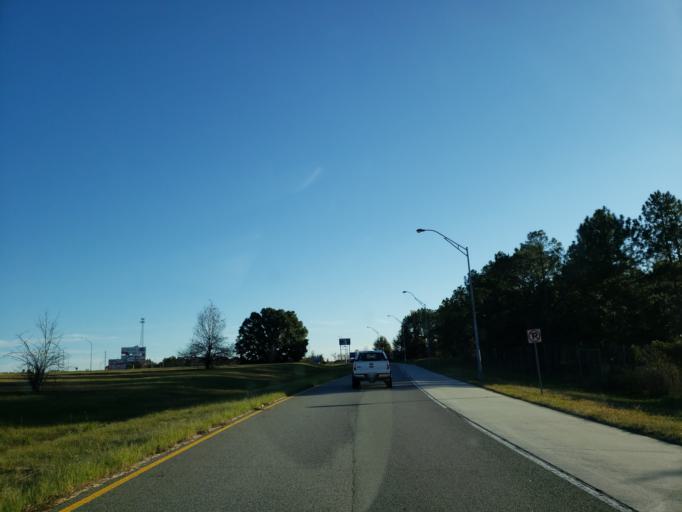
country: US
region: Georgia
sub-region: Dooly County
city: Unadilla
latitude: 32.2496
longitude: -83.7453
